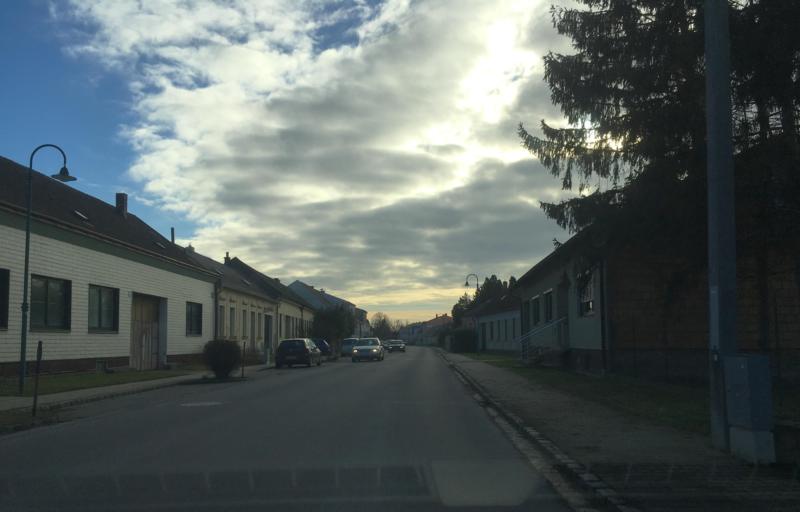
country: AT
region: Lower Austria
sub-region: Politischer Bezirk Ganserndorf
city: Eckartsau
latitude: 48.1478
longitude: 16.7949
